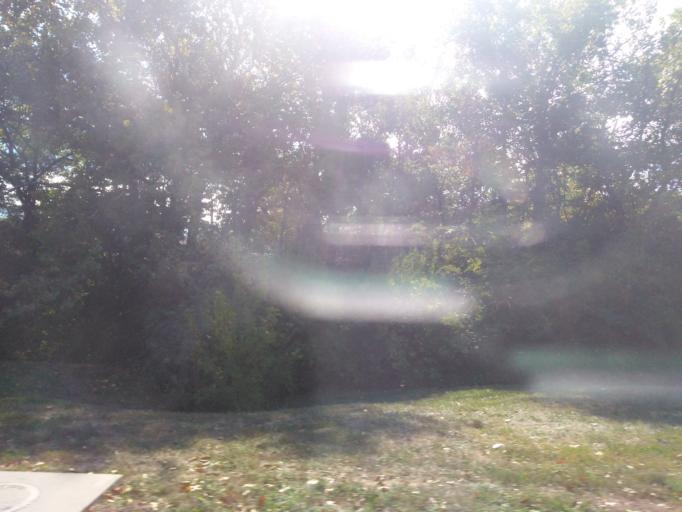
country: US
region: Missouri
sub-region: Saint Louis County
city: Concord
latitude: 38.4990
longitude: -90.3713
